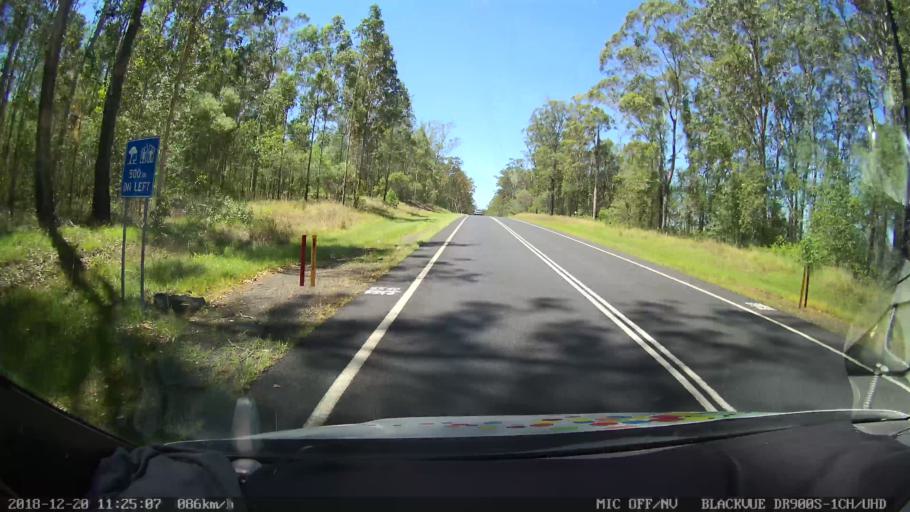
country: AU
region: New South Wales
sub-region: Richmond Valley
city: Casino
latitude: -29.0835
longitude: 153.0005
